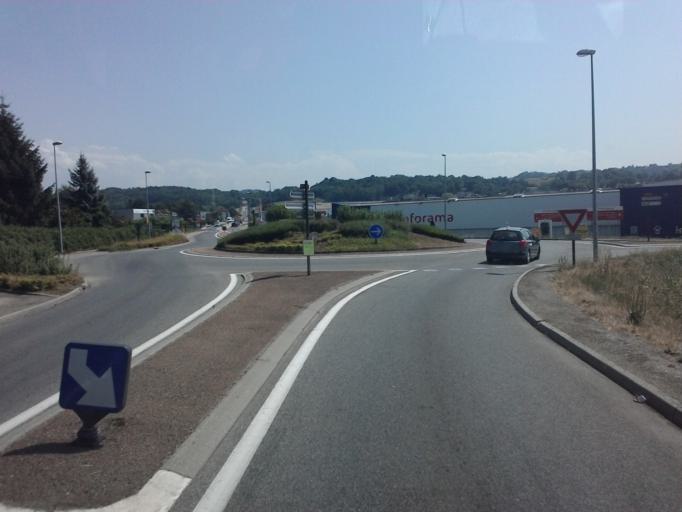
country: FR
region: Rhone-Alpes
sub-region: Departement de l'Isere
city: Les Abrets
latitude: 45.5322
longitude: 5.5874
